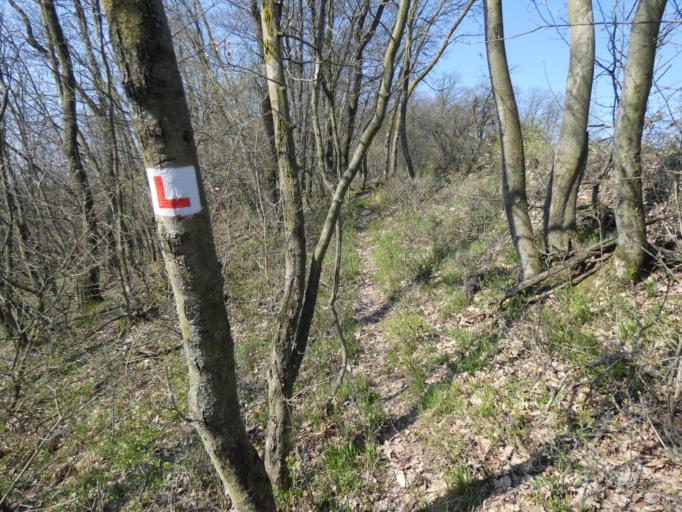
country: HU
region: Pest
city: Szob
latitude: 47.8617
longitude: 18.8564
